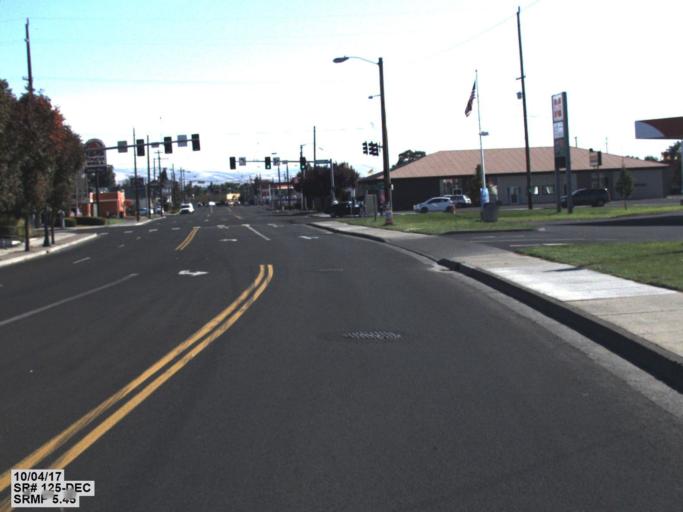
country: US
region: Washington
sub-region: Walla Walla County
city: Walla Walla
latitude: 46.0644
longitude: -118.3496
